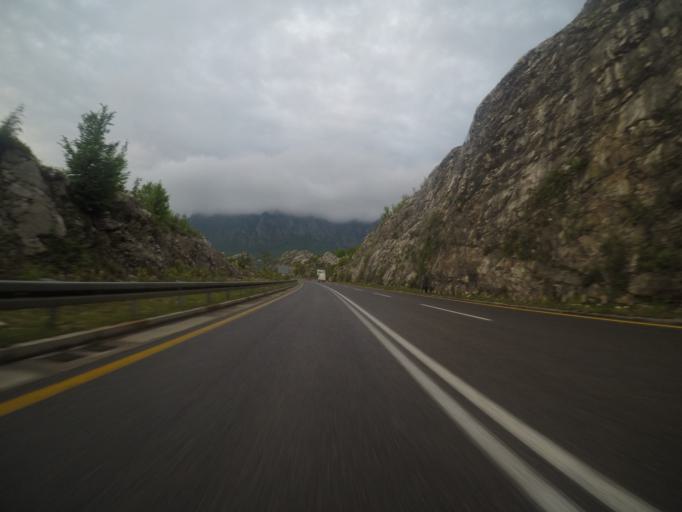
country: ME
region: Bar
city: Sutomore
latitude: 42.2112
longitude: 19.0480
